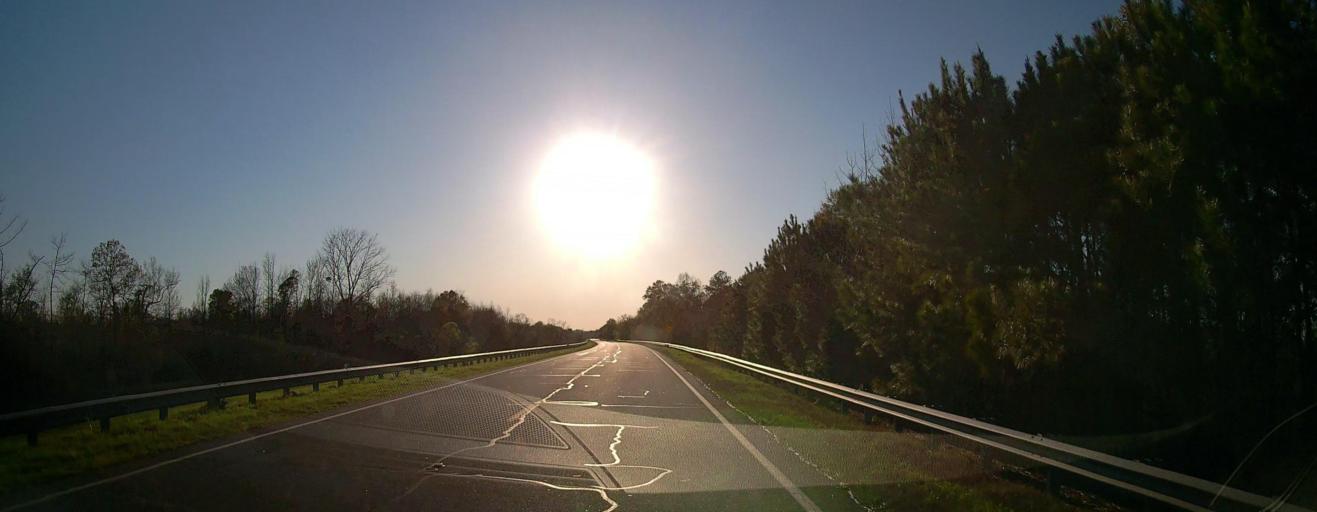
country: US
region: Georgia
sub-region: Wilcox County
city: Abbeville
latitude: 31.9984
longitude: -83.2687
